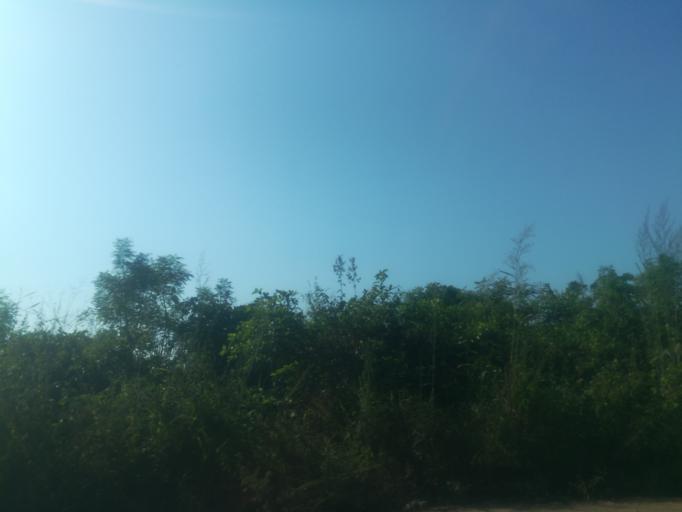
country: NG
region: Ogun
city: Abeokuta
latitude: 7.1498
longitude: 3.2590
